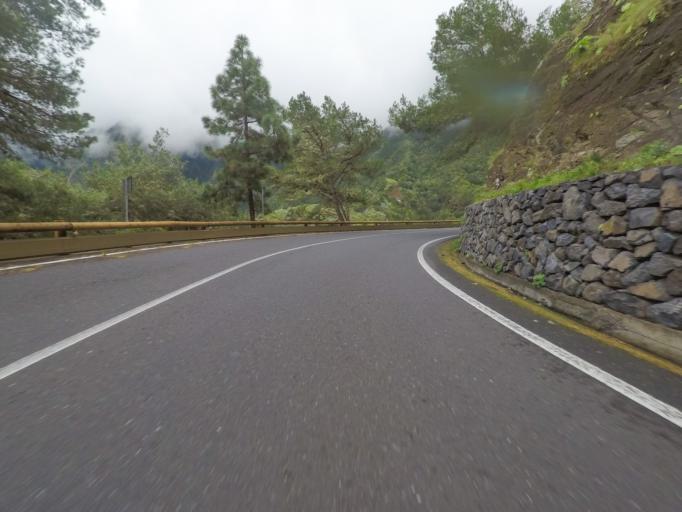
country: ES
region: Canary Islands
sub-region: Provincia de Santa Cruz de Tenerife
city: Hermigua
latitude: 28.1367
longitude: -17.1976
